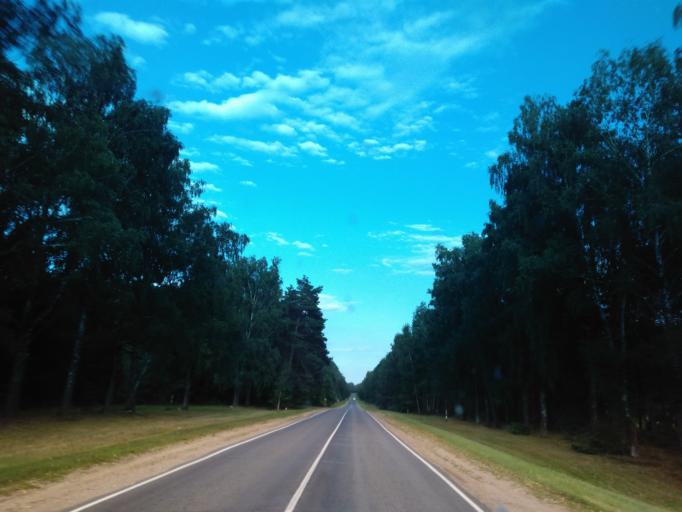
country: BY
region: Minsk
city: Uzda
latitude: 53.4254
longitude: 27.3716
